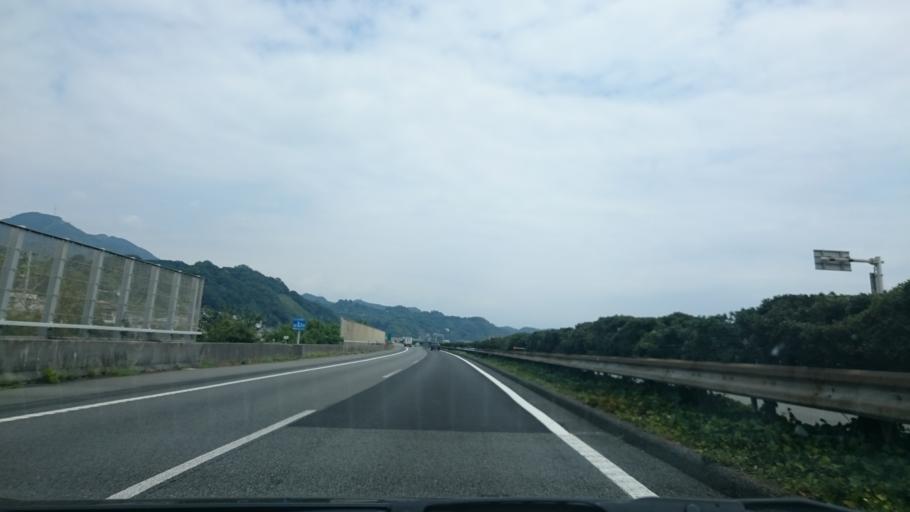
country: JP
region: Shizuoka
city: Fujinomiya
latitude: 35.1073
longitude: 138.5694
